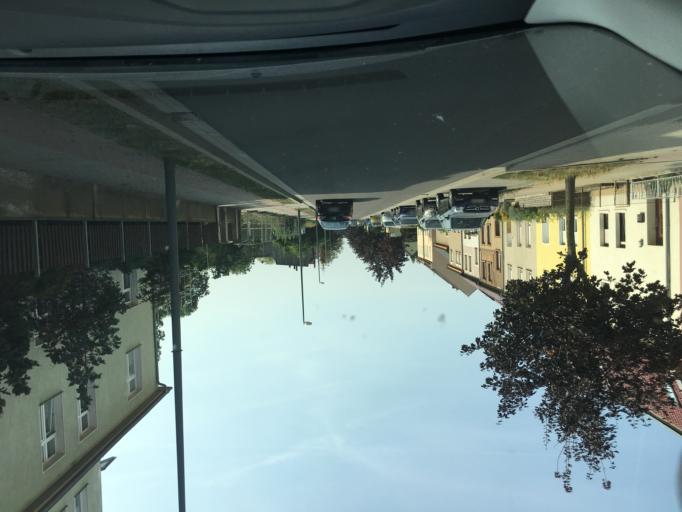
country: DE
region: Saxony-Anhalt
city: Nienburg/Saale
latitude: 51.8460
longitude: 11.7663
